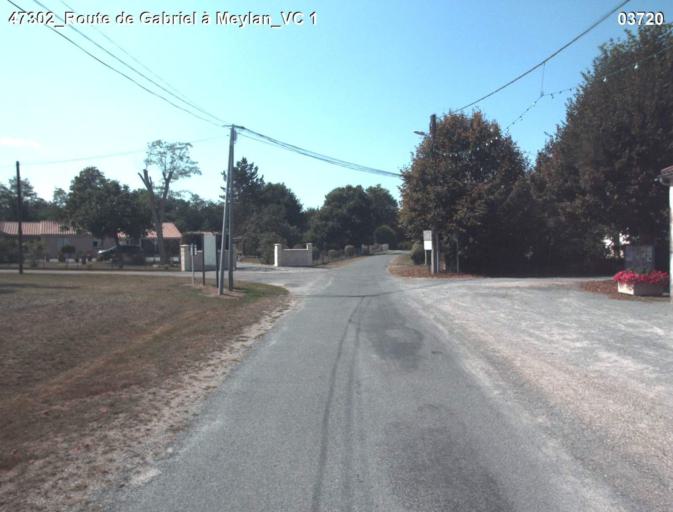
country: FR
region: Aquitaine
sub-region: Departement du Lot-et-Garonne
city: Mezin
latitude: 44.0755
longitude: 0.1197
